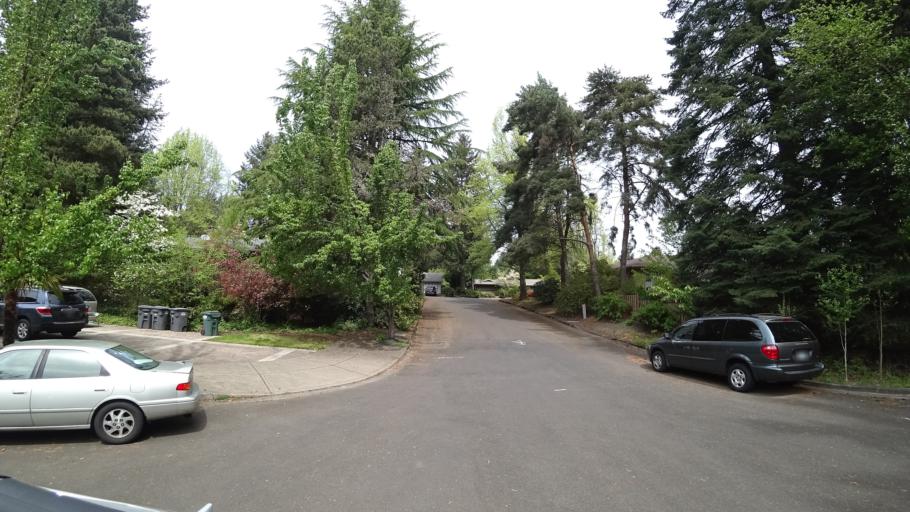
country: US
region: Oregon
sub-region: Washington County
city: Hillsboro
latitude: 45.5082
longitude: -122.9474
